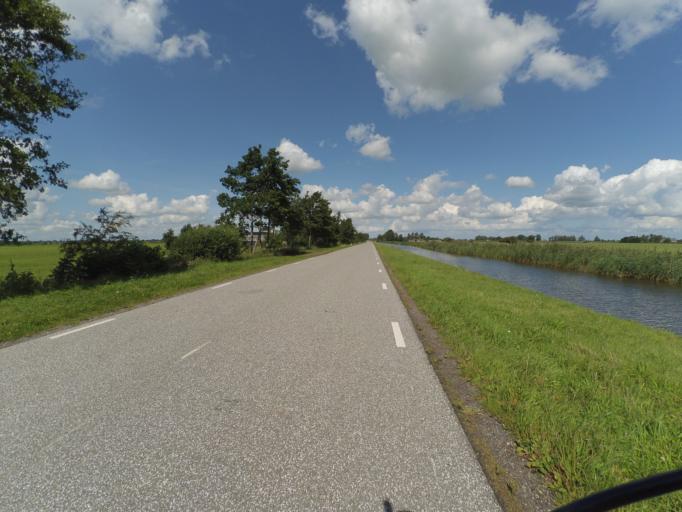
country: NL
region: Friesland
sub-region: Gemeente Achtkarspelen
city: Buitenpost
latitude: 53.2522
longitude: 6.1828
